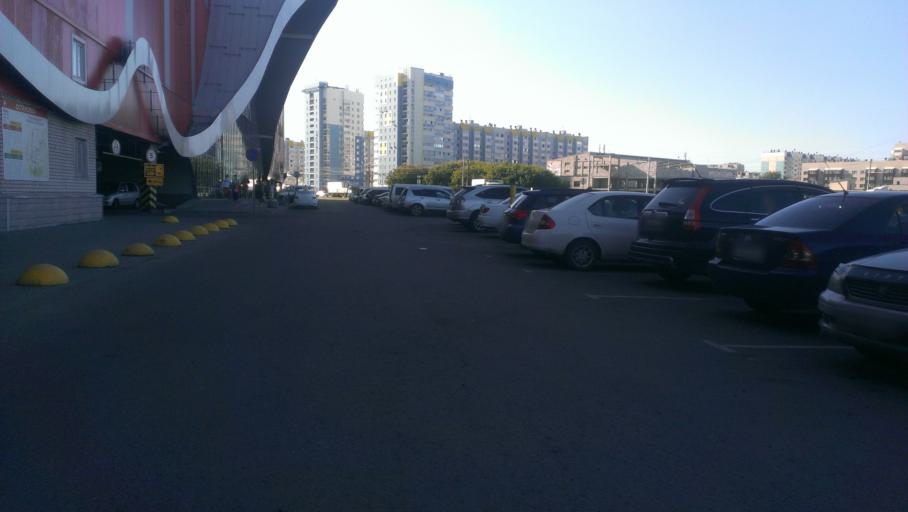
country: RU
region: Altai Krai
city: Novosilikatnyy
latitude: 53.3263
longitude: 83.6919
